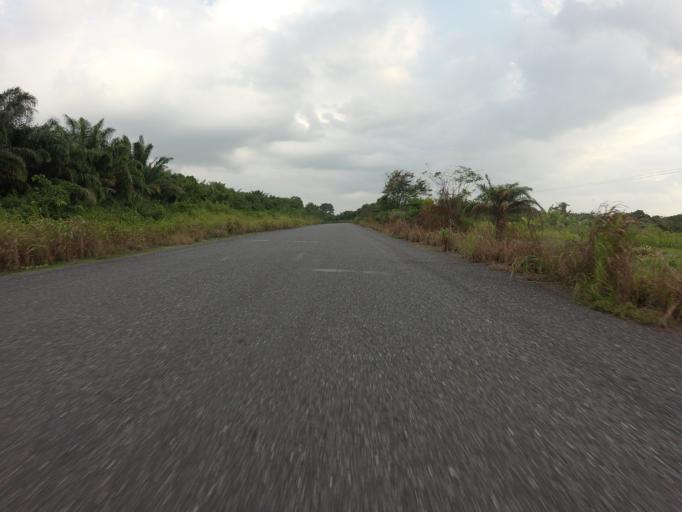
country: GH
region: Volta
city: Ho
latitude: 6.4981
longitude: 0.4871
